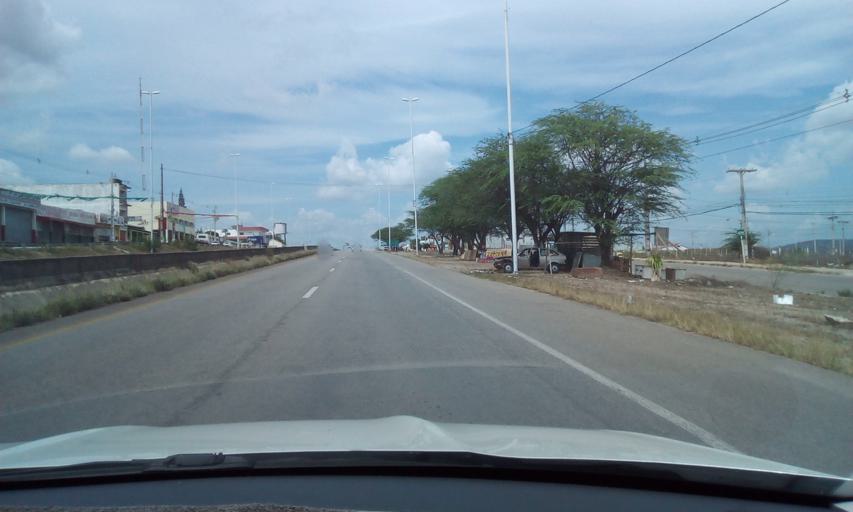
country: BR
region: Pernambuco
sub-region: Bezerros
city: Bezerros
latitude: -8.2432
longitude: -35.7525
